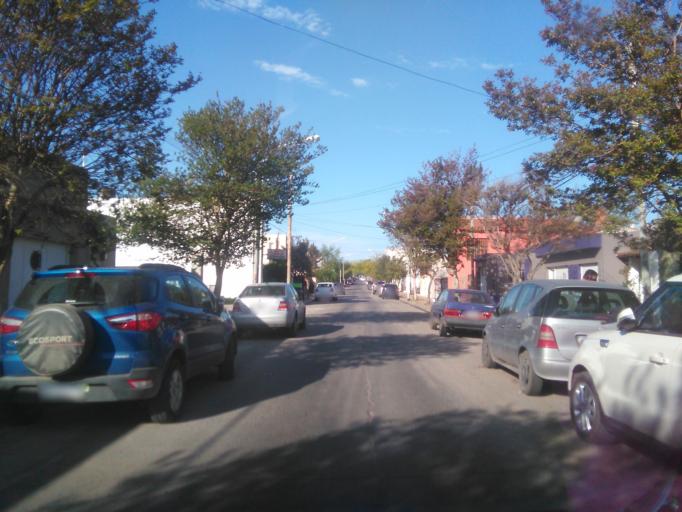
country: AR
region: Buenos Aires
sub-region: Partido de Tandil
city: Tandil
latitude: -37.3293
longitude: -59.1255
